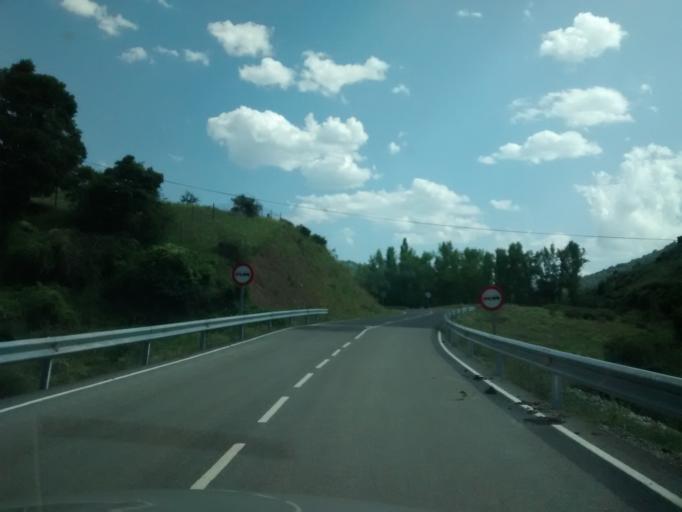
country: ES
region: La Rioja
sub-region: Provincia de La Rioja
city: Rabanera
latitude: 42.1906
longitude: -2.4847
